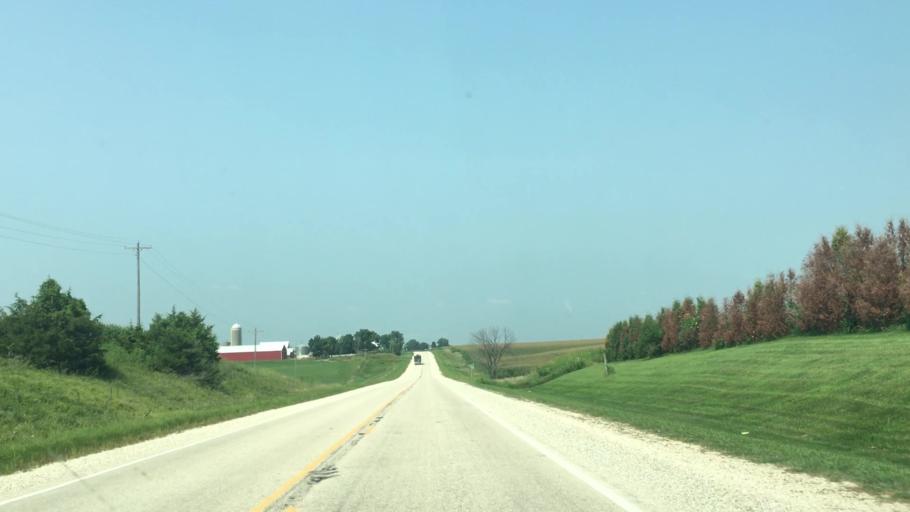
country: US
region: Iowa
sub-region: Fayette County
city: West Union
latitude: 43.0094
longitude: -91.8242
